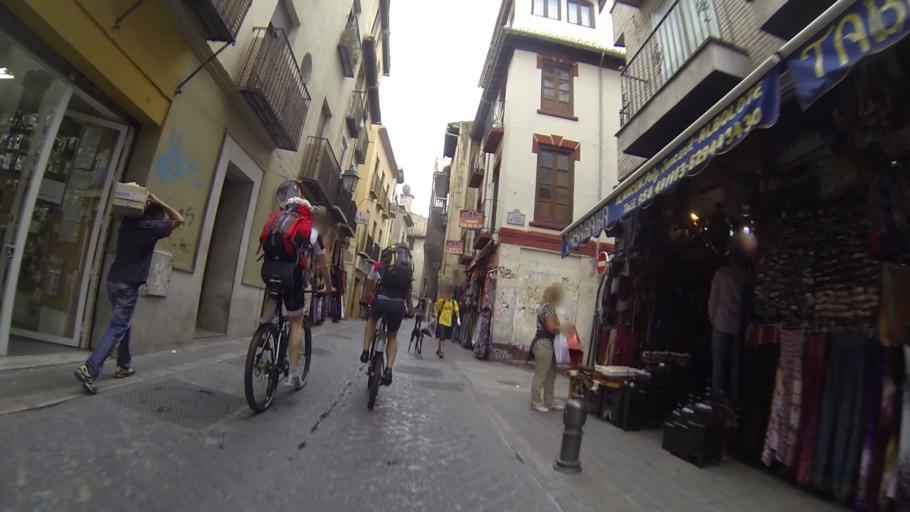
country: ES
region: Andalusia
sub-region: Provincia de Granada
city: Granada
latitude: 37.1786
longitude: -3.5981
